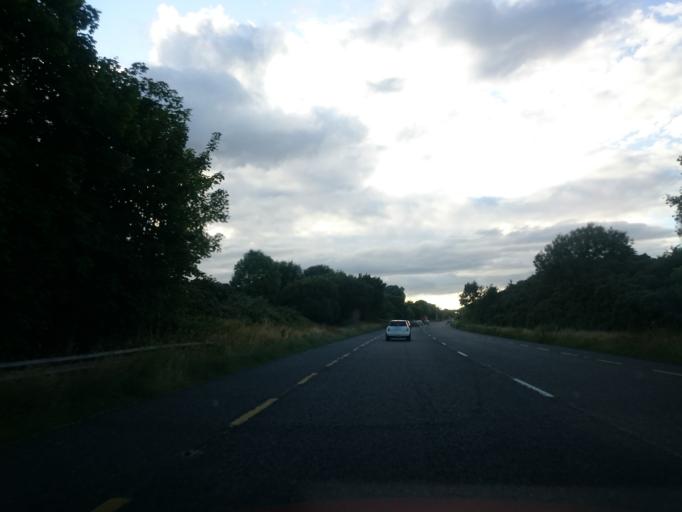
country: IE
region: Leinster
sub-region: Loch Garman
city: Loch Garman
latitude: 52.3060
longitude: -6.4777
